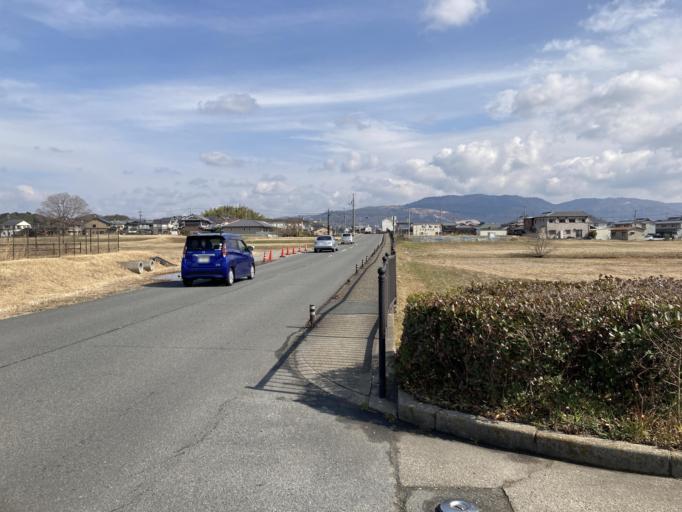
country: JP
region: Nara
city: Nara-shi
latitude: 34.6941
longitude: 135.8004
